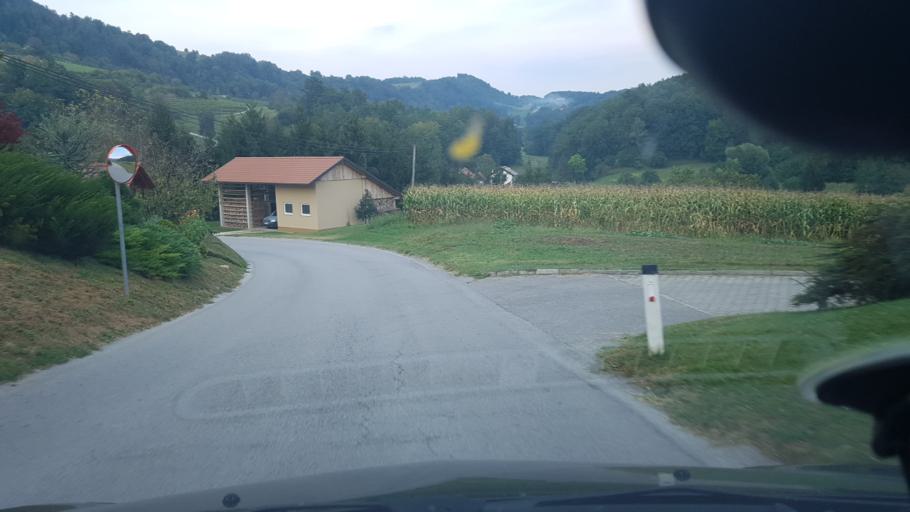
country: SI
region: Krsko
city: Senovo
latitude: 46.0081
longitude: 15.4890
